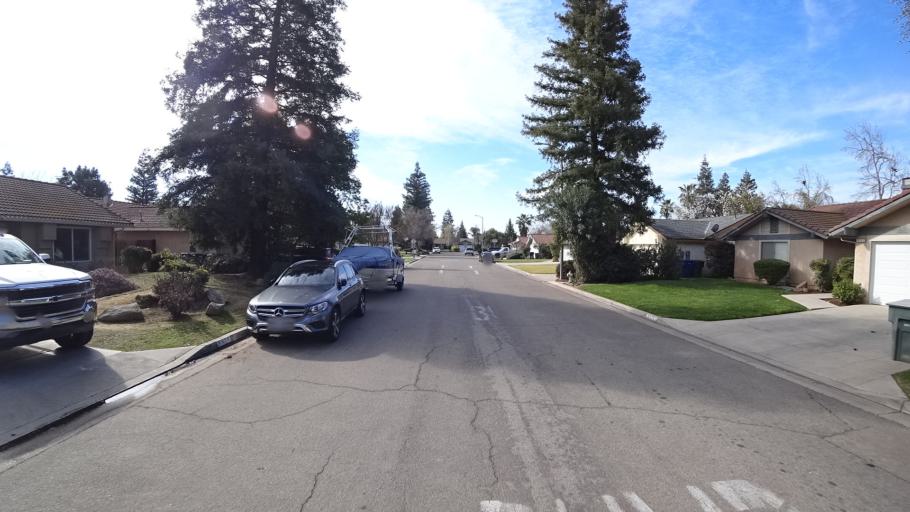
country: US
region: California
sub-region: Fresno County
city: West Park
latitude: 36.8323
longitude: -119.8696
